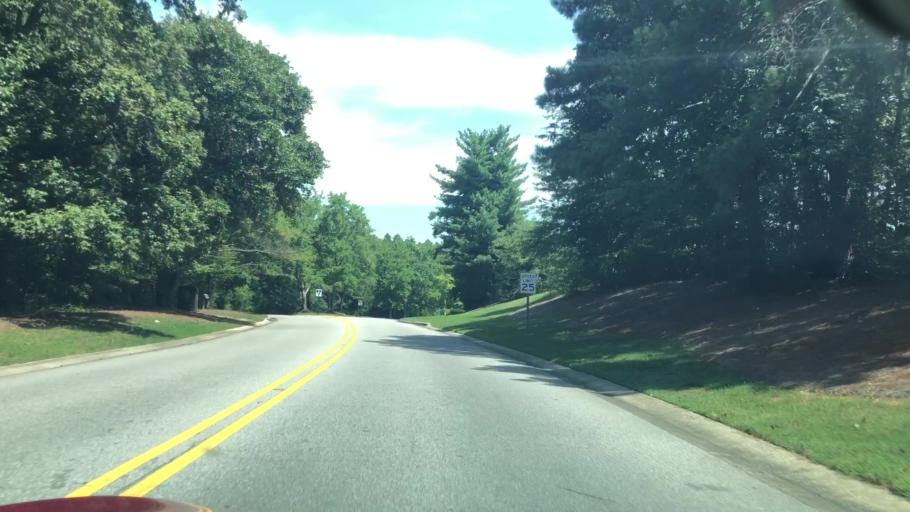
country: US
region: Alabama
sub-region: Shelby County
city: Meadowbrook
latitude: 33.4138
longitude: -86.6886
